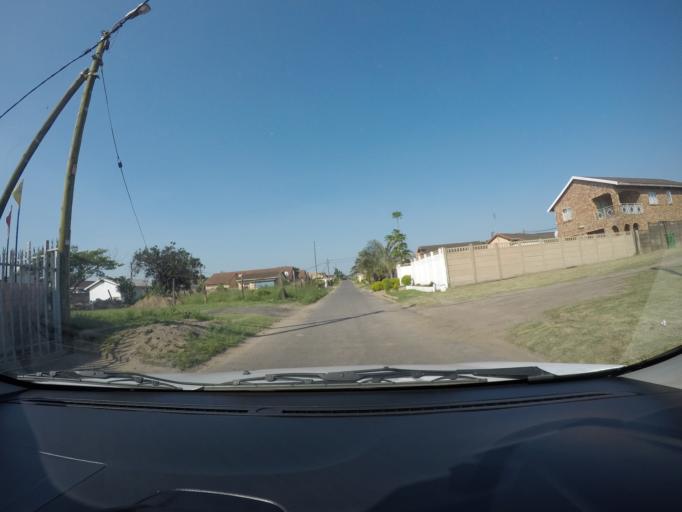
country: ZA
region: KwaZulu-Natal
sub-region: uThungulu District Municipality
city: Richards Bay
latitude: -28.7220
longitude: 32.0379
